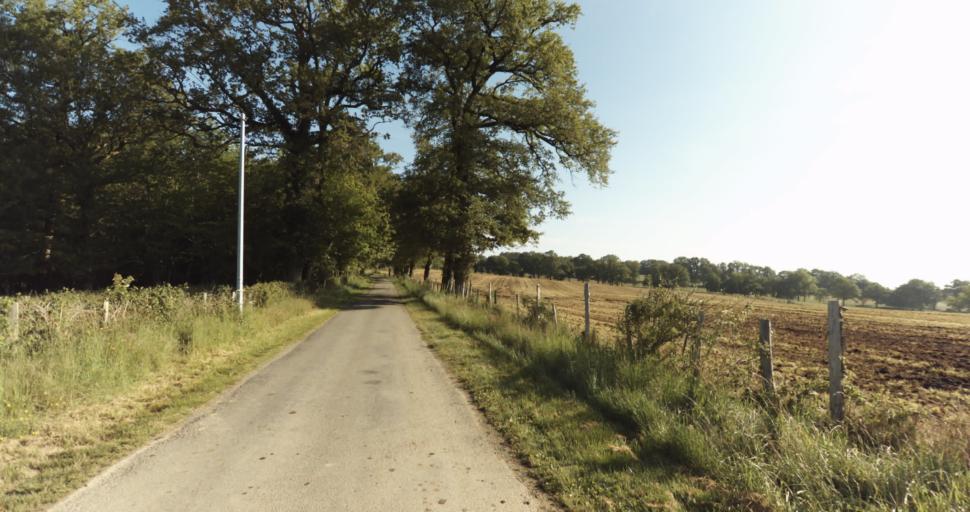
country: FR
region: Limousin
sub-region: Departement de la Haute-Vienne
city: Solignac
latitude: 45.7318
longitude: 1.2604
